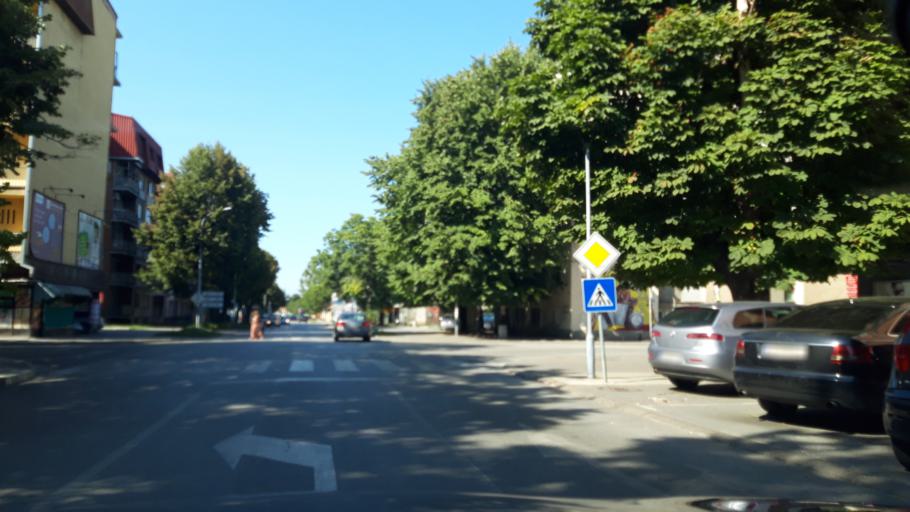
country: RS
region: Autonomna Pokrajina Vojvodina
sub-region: Sremski Okrug
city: Ruma
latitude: 45.0090
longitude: 19.8227
